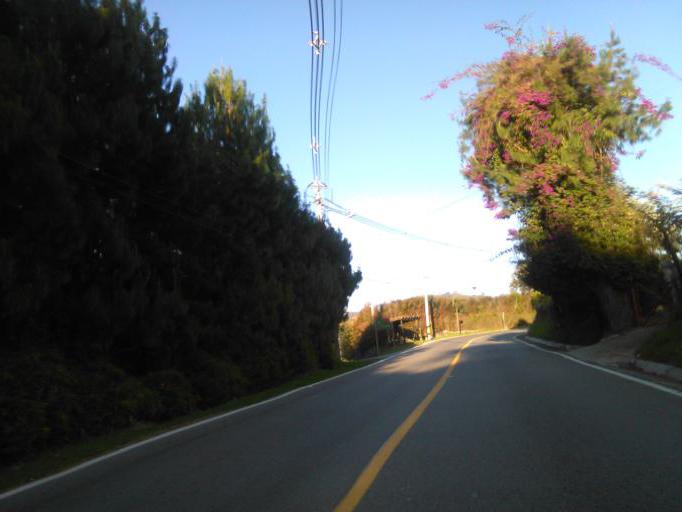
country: CO
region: Antioquia
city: La Ceja
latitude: 6.0079
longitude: -75.3967
